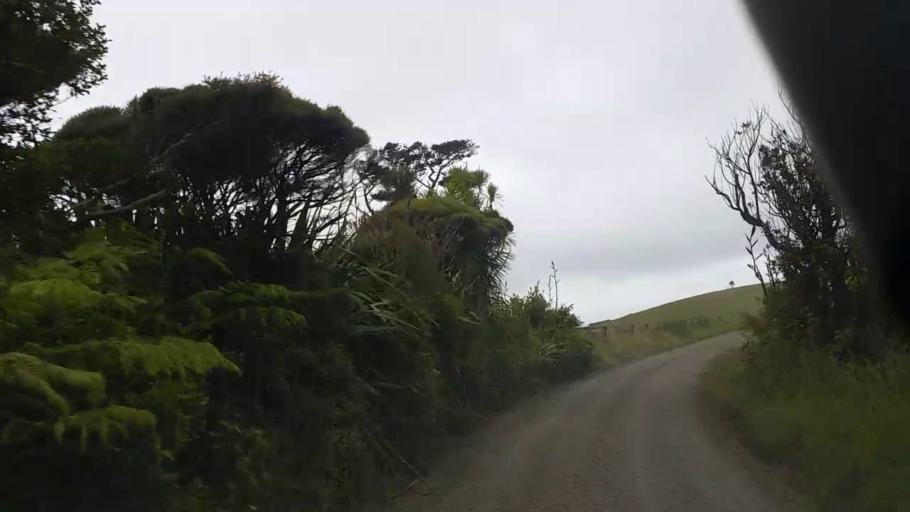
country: NZ
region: Auckland
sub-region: Auckland
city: Muriwai Beach
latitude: -36.9291
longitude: 174.4681
